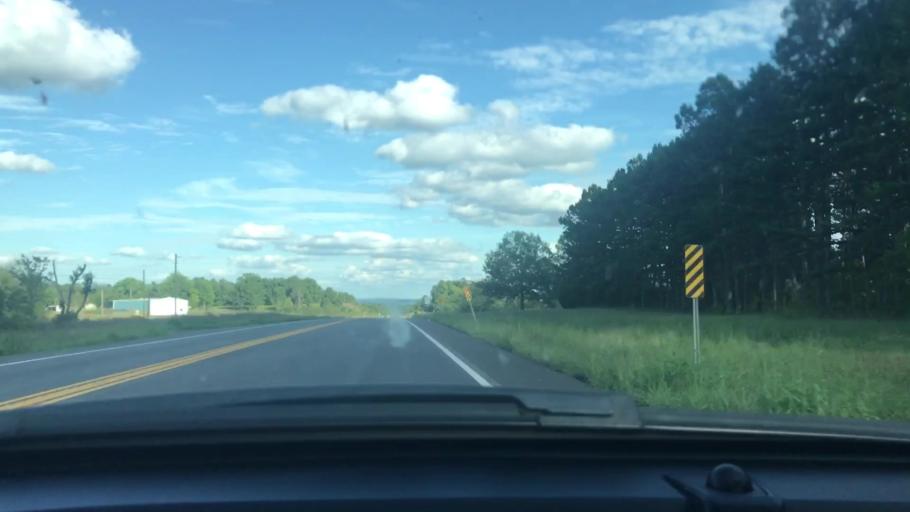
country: US
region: Missouri
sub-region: Oregon County
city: Thayer
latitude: 36.5834
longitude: -91.6109
